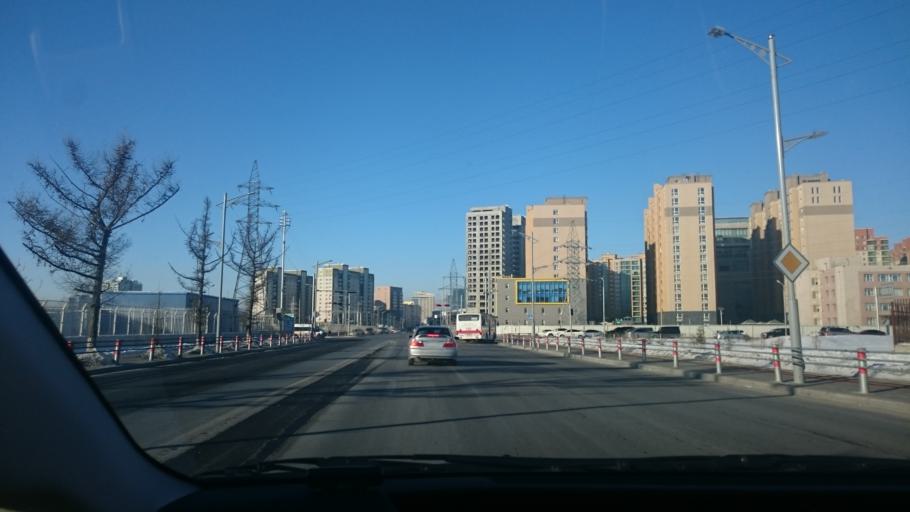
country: MN
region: Ulaanbaatar
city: Ulaanbaatar
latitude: 47.8990
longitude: 106.9316
